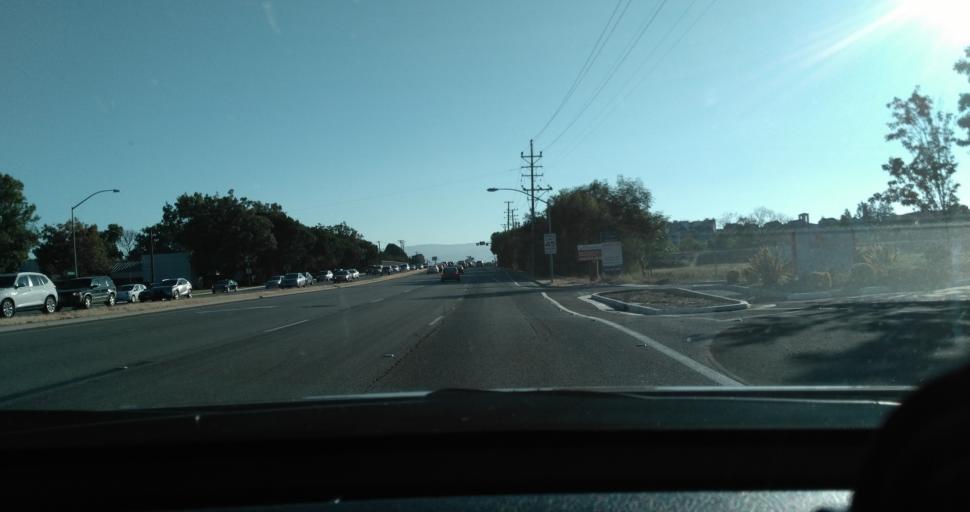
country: US
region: California
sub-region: Santa Clara County
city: Milpitas
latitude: 37.3968
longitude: -121.9381
